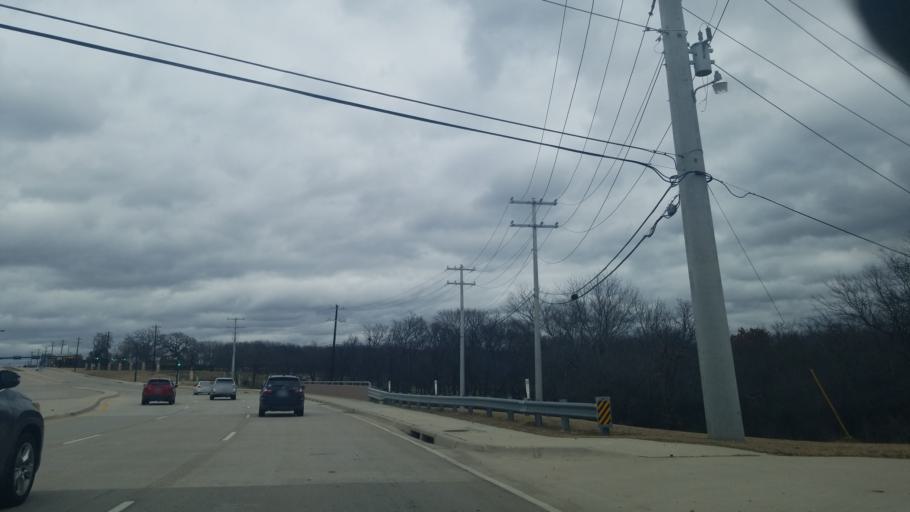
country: US
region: Texas
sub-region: Denton County
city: Bartonville
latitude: 33.0436
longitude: -97.1659
